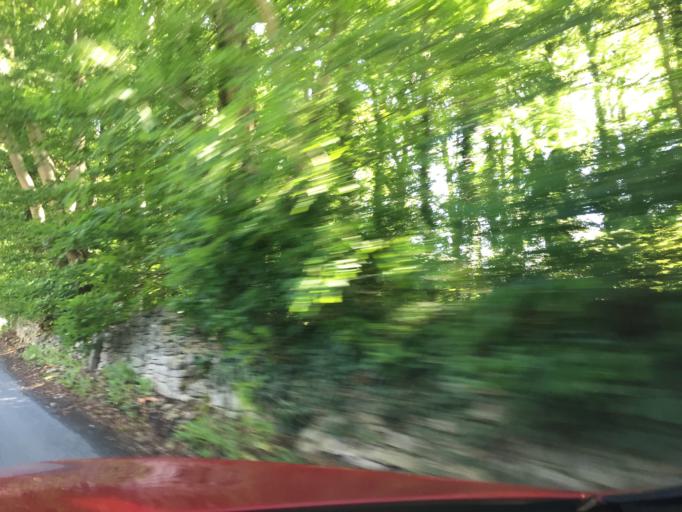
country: GB
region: England
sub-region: Gloucestershire
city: Stonehouse
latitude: 51.7632
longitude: -2.2461
